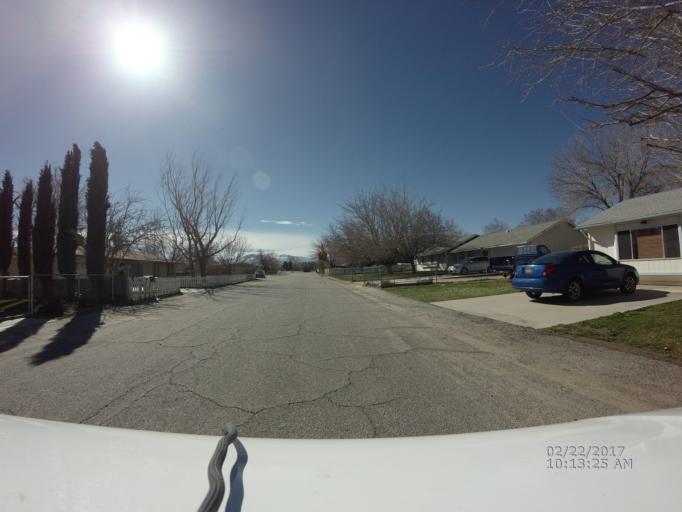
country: US
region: California
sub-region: Los Angeles County
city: Lake Los Angeles
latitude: 34.6261
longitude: -117.8283
